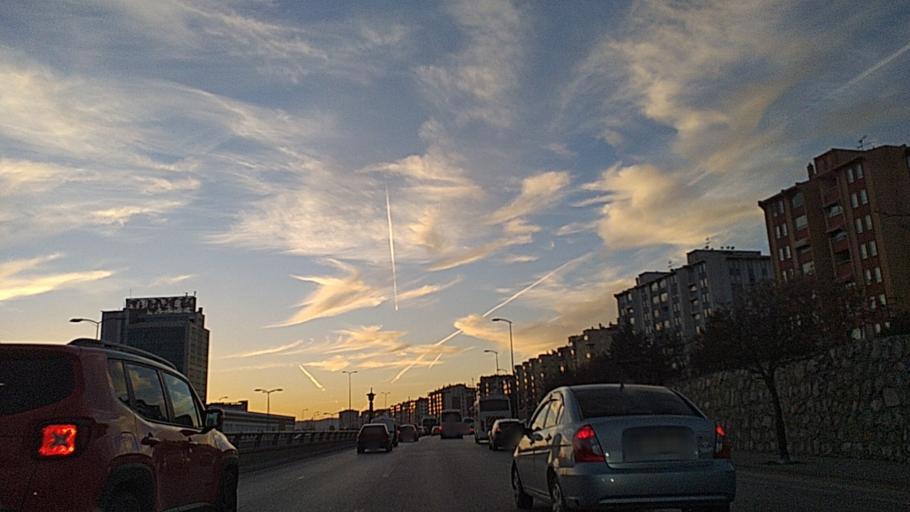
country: TR
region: Ankara
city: Etimesgut
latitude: 39.9676
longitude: 32.6276
